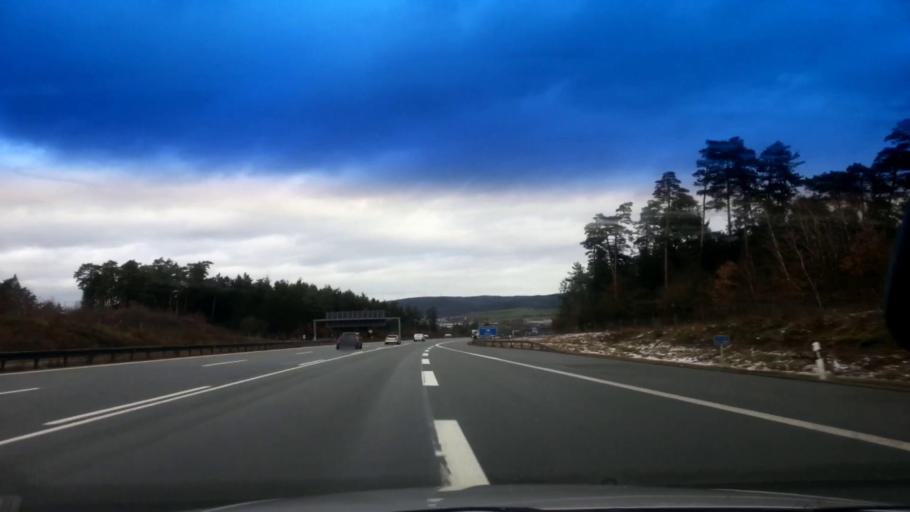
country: DE
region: Bavaria
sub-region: Upper Franconia
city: Himmelkron
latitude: 50.0328
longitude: 11.6074
